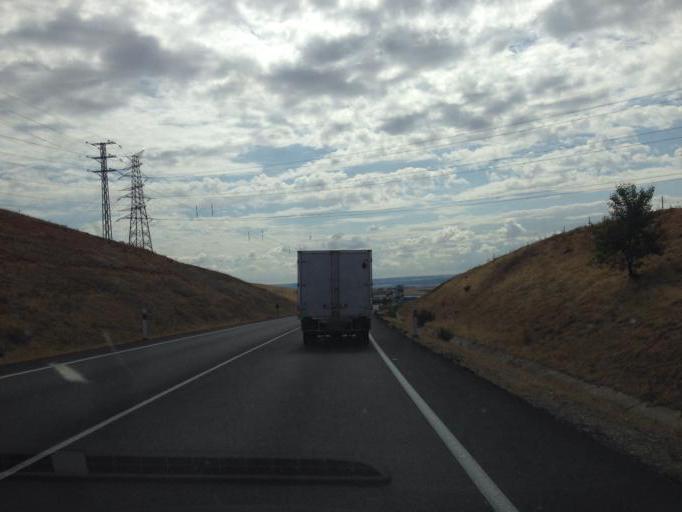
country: ES
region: Madrid
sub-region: Provincia de Madrid
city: Ajalvir
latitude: 40.5526
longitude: -3.4787
